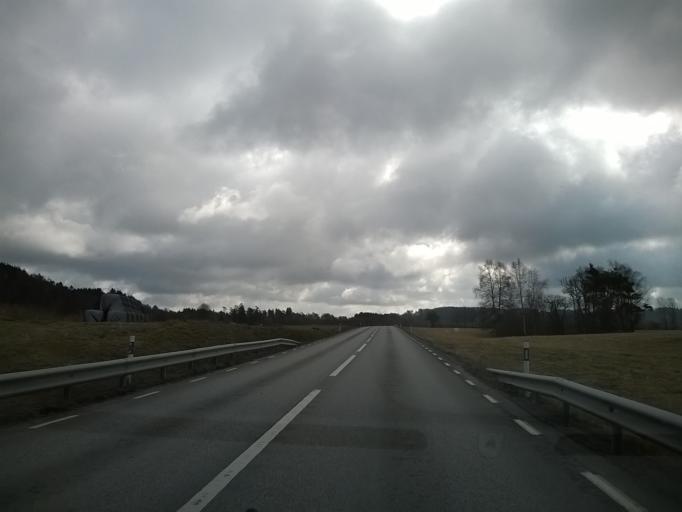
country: SE
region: Halland
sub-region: Varbergs Kommun
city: Tvaaker
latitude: 57.1444
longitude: 12.5080
